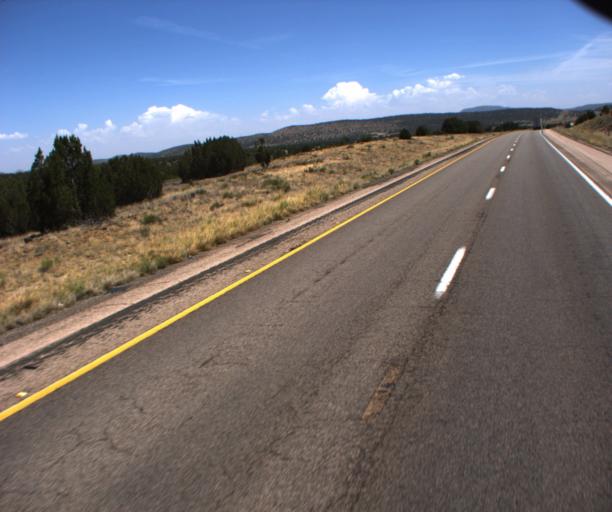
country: US
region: Arizona
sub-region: Mohave County
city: Peach Springs
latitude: 35.2233
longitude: -113.2406
